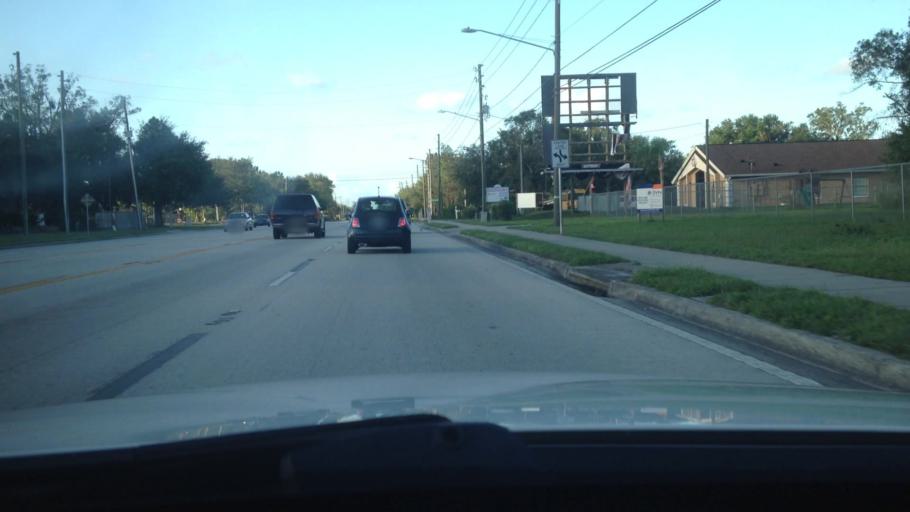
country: US
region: Florida
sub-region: Orange County
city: Union Park
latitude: 28.5583
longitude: -81.2859
